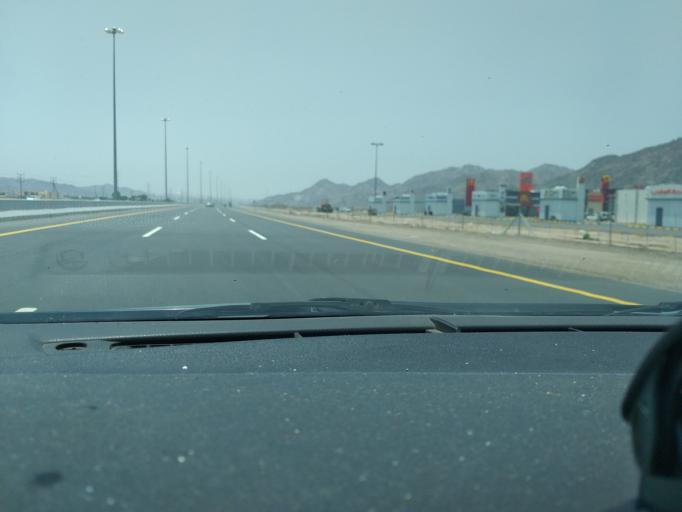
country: SA
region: Makkah
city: Al Hada
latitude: 21.3550
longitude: 40.1157
